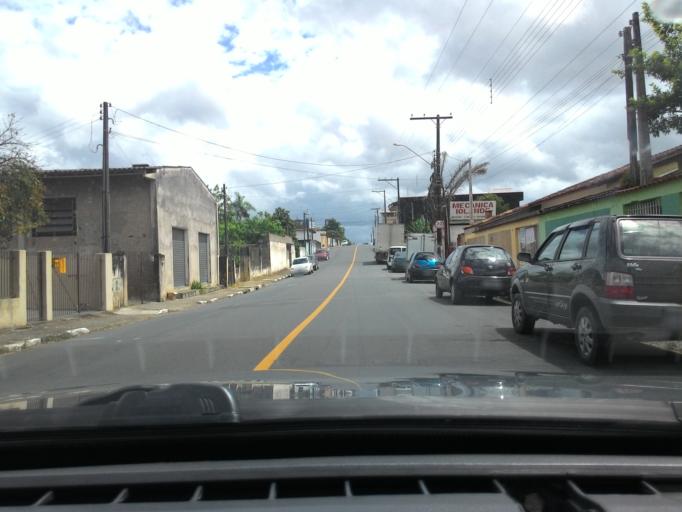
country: BR
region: Sao Paulo
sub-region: Registro
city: Registro
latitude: -24.5017
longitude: -47.8435
